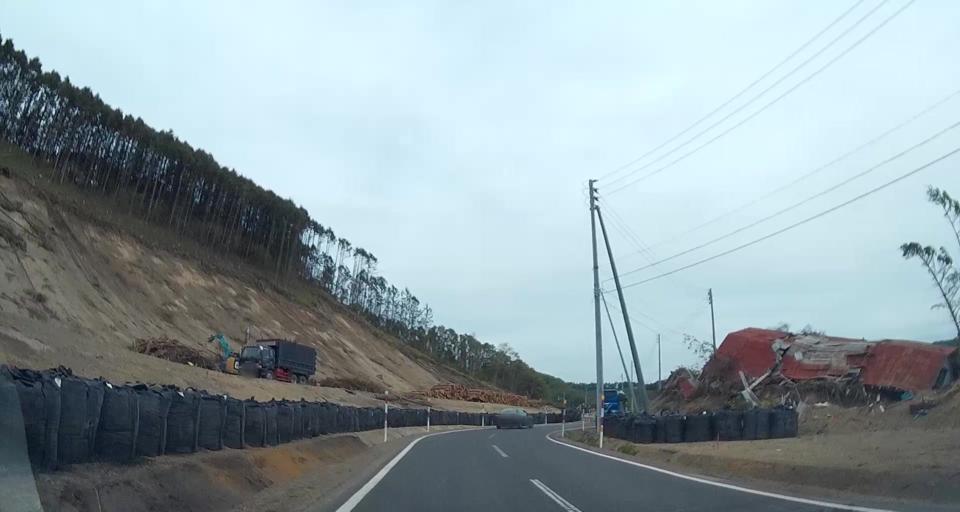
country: JP
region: Hokkaido
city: Chitose
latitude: 42.7520
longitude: 141.9143
